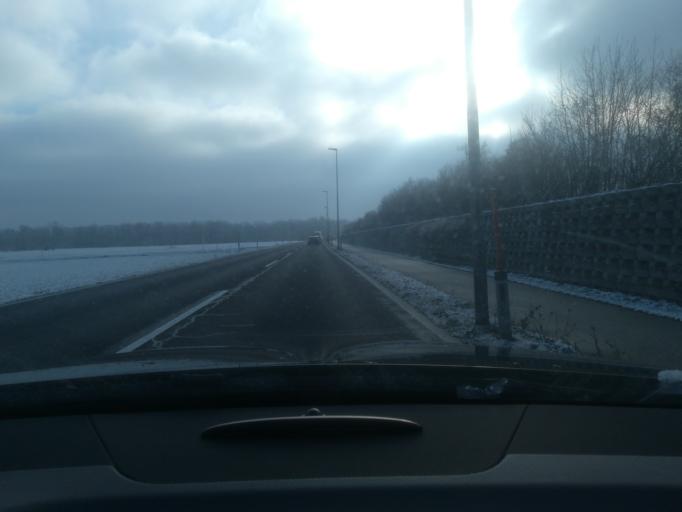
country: AT
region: Upper Austria
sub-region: Wels-Land
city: Marchtrenk
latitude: 48.1829
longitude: 14.1201
